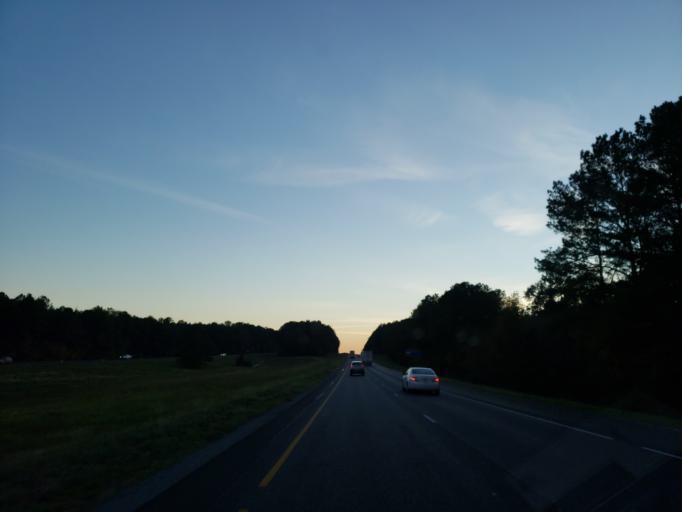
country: US
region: Alabama
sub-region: Sumter County
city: York
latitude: 32.5365
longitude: -88.2854
